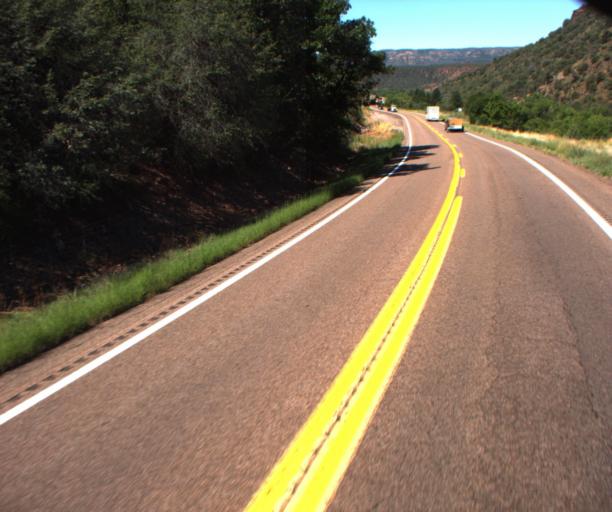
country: US
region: Arizona
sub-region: Navajo County
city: Cibecue
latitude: 34.0022
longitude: -110.2691
